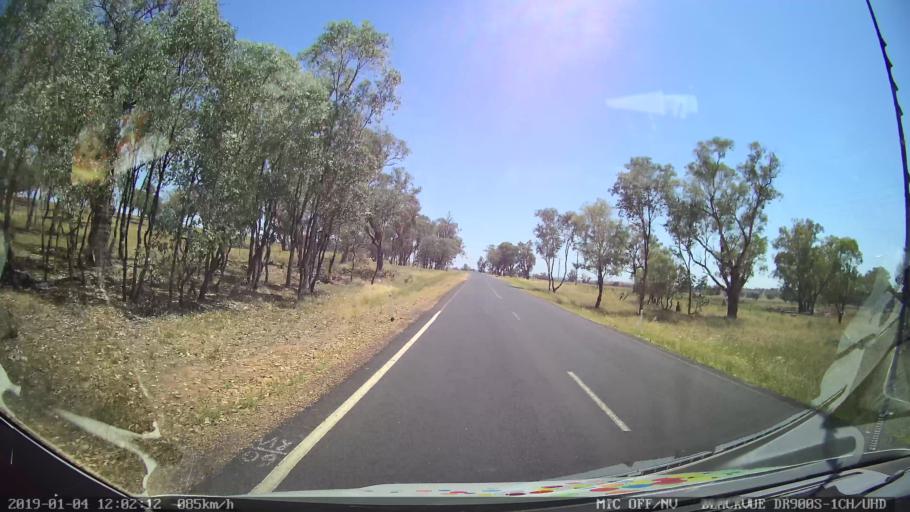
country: AU
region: New South Wales
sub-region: Wellington
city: Wellington
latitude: -32.7816
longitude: 148.6862
